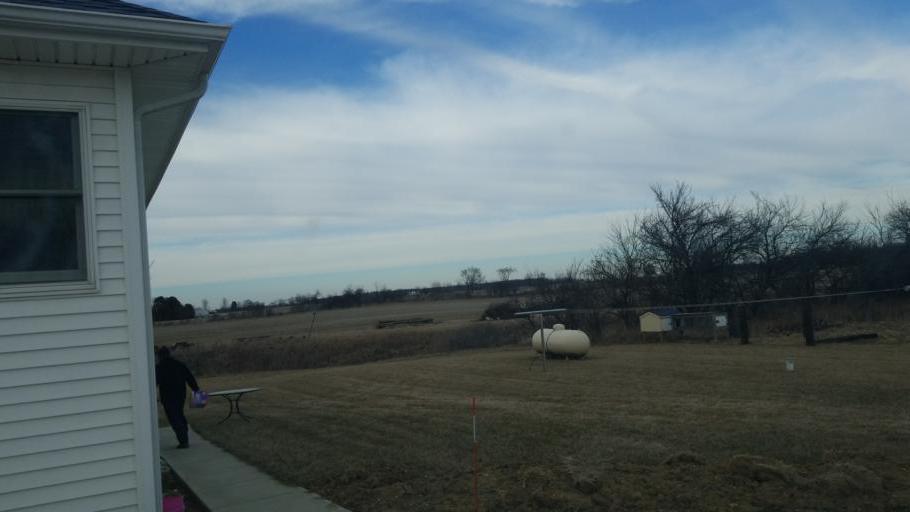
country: US
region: Ohio
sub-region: Defiance County
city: Hicksville
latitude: 41.3592
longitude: -84.7857
